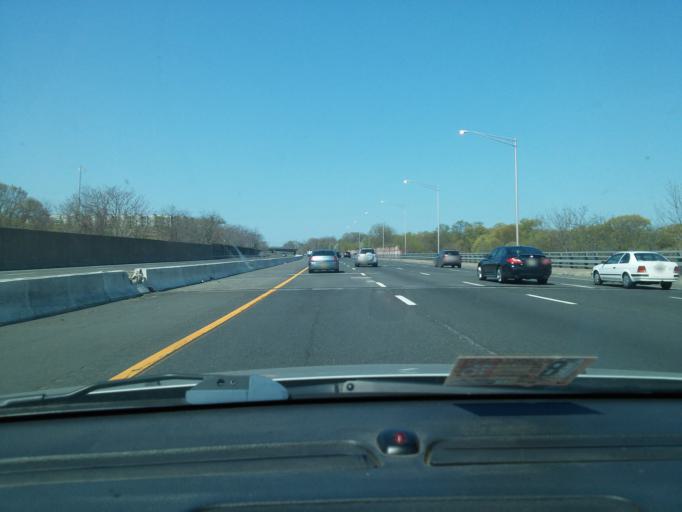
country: US
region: New Jersey
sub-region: Union County
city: Springfield
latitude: 40.7120
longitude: -74.3231
